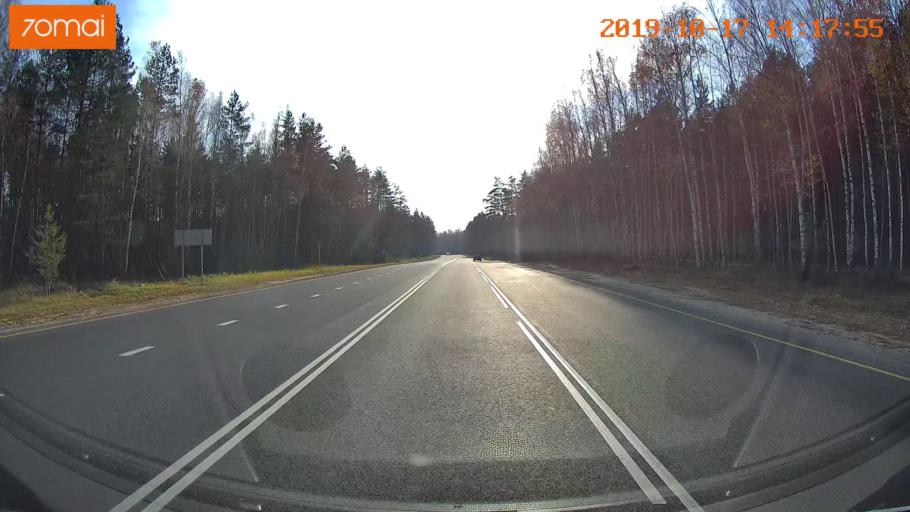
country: RU
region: Rjazan
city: Spas-Klepiki
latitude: 55.0697
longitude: 40.0350
